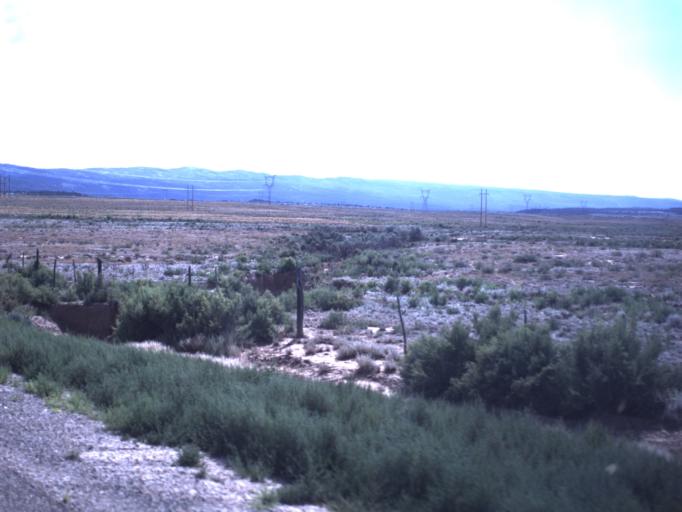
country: US
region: Utah
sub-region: Duchesne County
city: Duchesne
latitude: 40.2243
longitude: -110.7227
